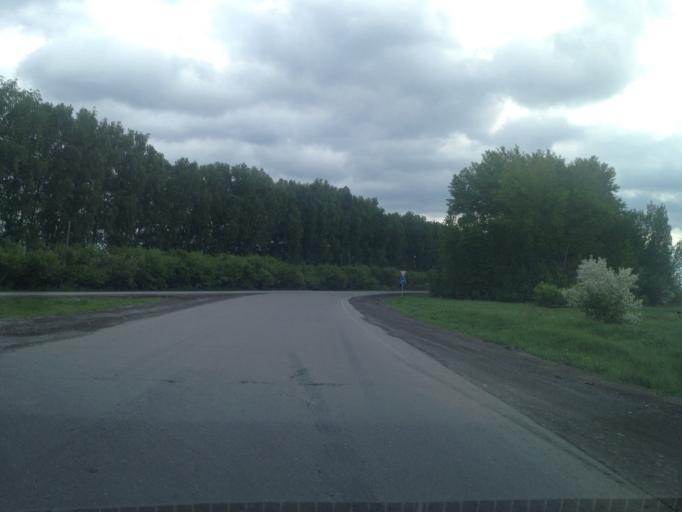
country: RU
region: Sverdlovsk
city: Aramil
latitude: 56.6943
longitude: 60.7646
